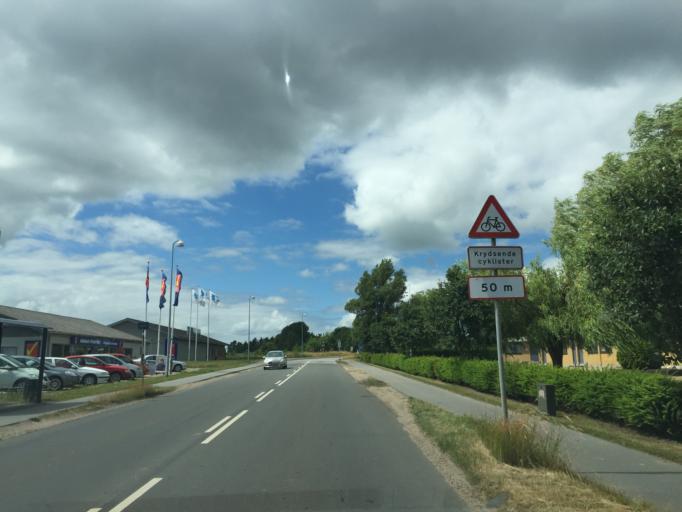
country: DK
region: South Denmark
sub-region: Svendborg Kommune
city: Svendborg
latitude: 55.0696
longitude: 10.5716
